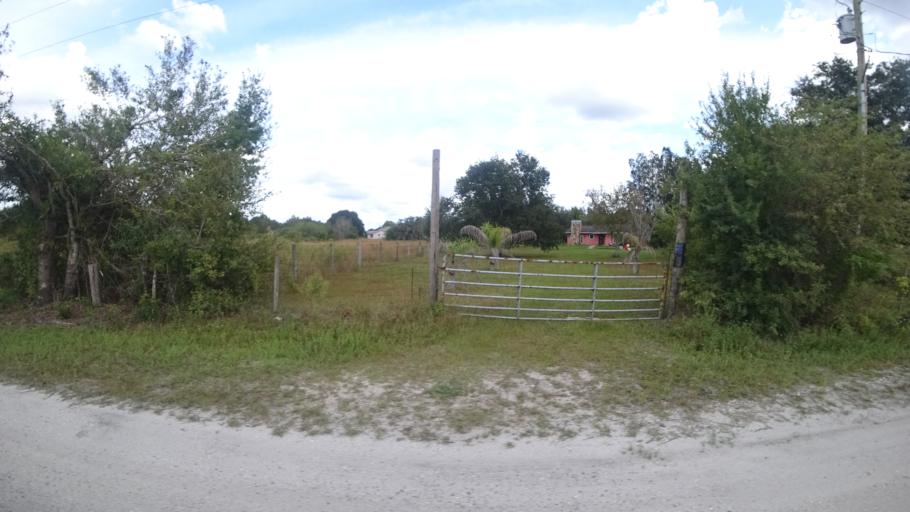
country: US
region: Florida
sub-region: Sarasota County
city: Lake Sarasota
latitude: 27.4001
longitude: -82.2664
